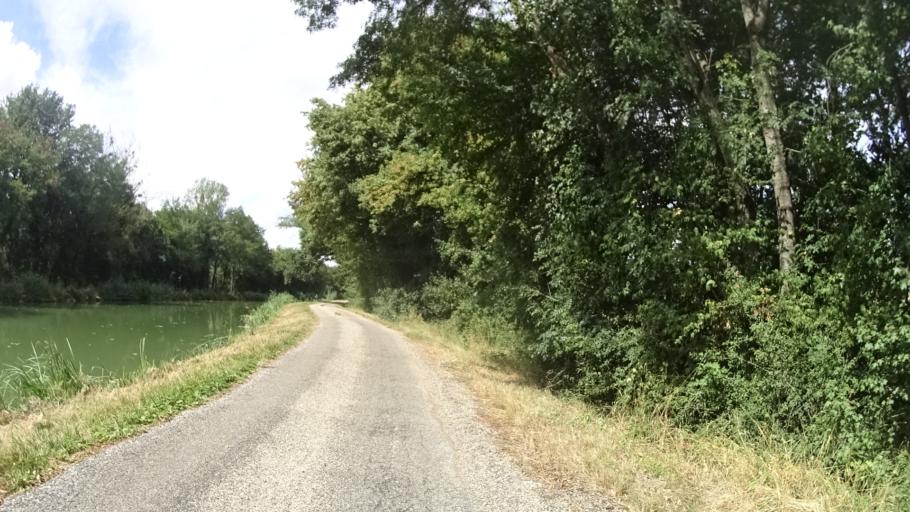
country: FR
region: Franche-Comte
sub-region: Departement du Jura
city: Saint-Aubin
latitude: 47.0911
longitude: 5.3270
